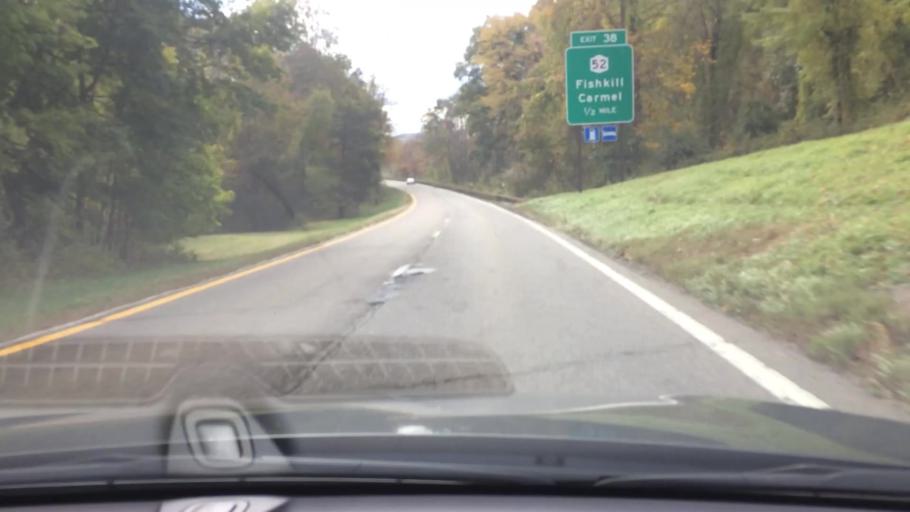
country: US
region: New York
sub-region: Dutchess County
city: Hillside Lake
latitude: 41.5668
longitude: -73.7822
